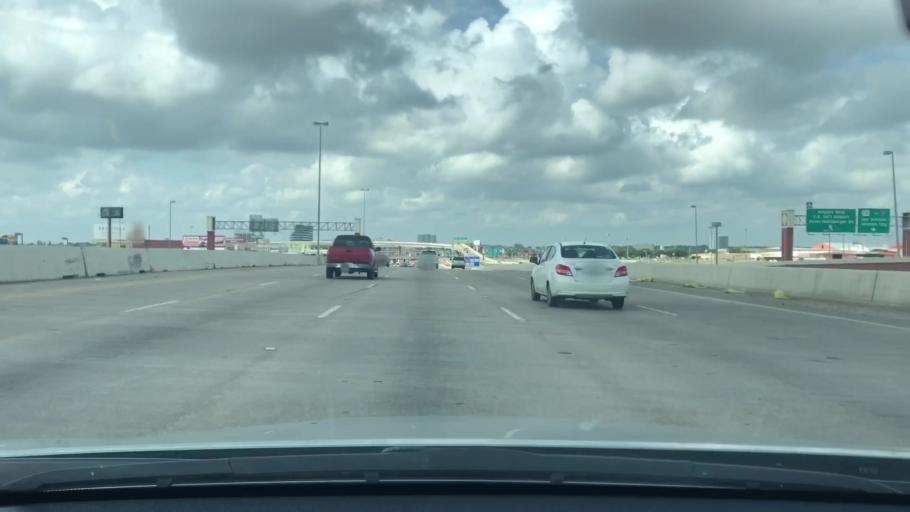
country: US
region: Texas
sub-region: Bexar County
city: Alamo Heights
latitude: 29.5182
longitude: -98.4688
